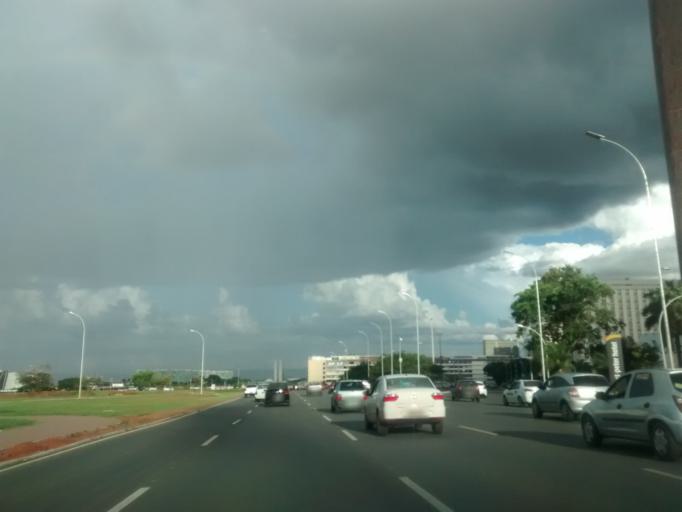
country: BR
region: Federal District
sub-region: Brasilia
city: Brasilia
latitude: -15.7934
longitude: -47.8888
